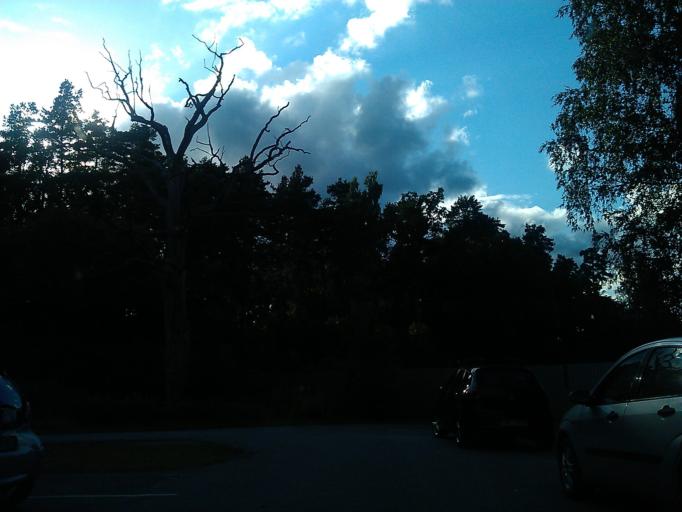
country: LV
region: Stopini
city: Ulbroka
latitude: 56.9653
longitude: 24.2869
